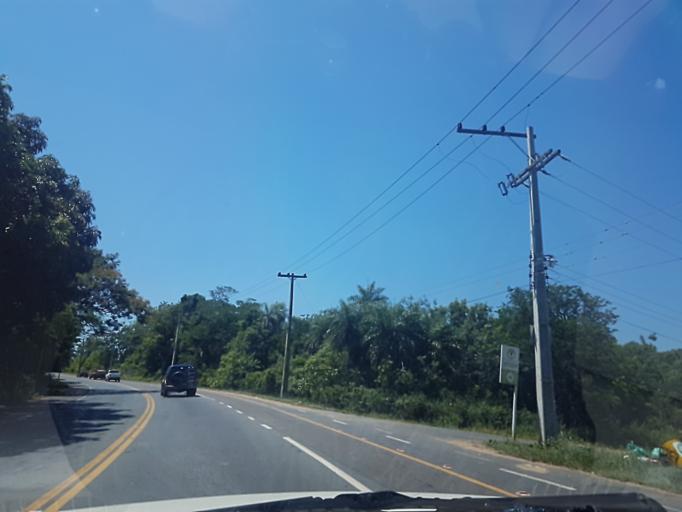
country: PY
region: Cordillera
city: San Bernardino
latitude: -25.2839
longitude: -57.3168
